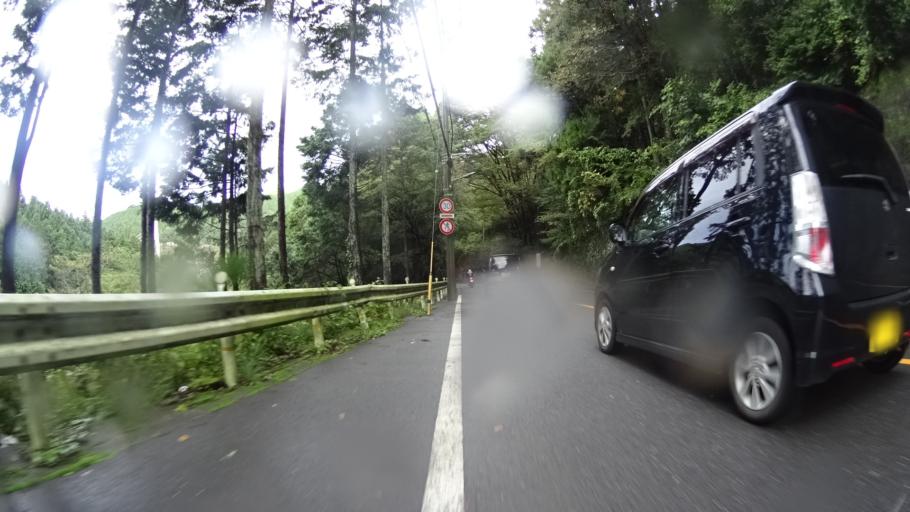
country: JP
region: Tokyo
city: Ome
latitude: 35.8101
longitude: 139.1687
